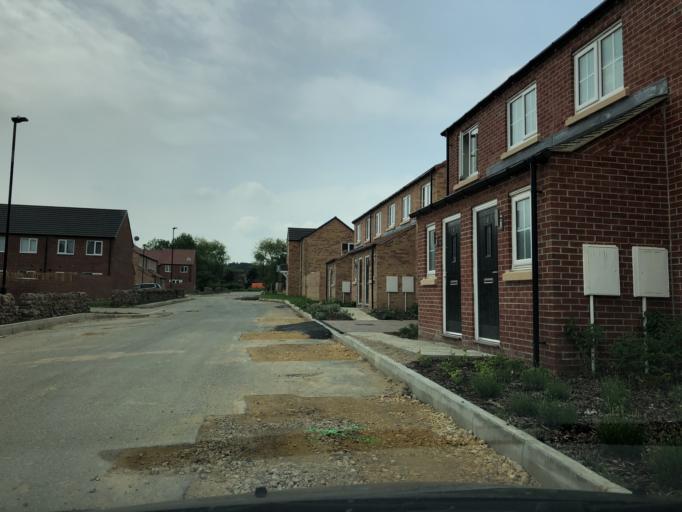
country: GB
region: England
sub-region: North Yorkshire
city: Harrogate
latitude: 54.0081
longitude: -1.5670
